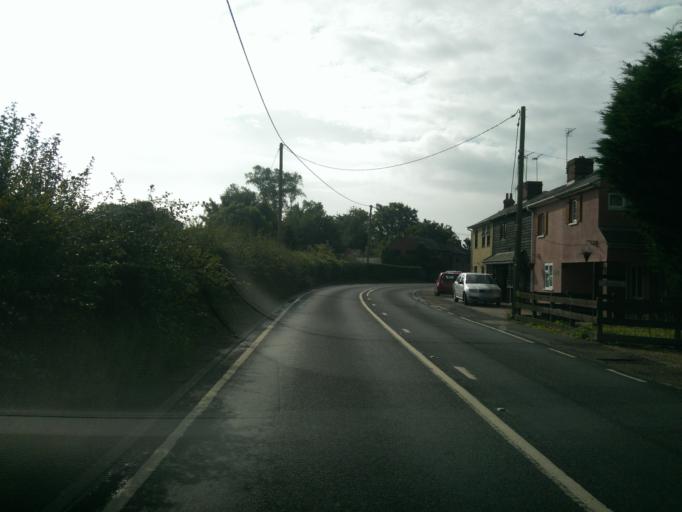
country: GB
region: England
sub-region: Essex
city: Little Clacton
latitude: 51.8421
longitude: 1.1283
